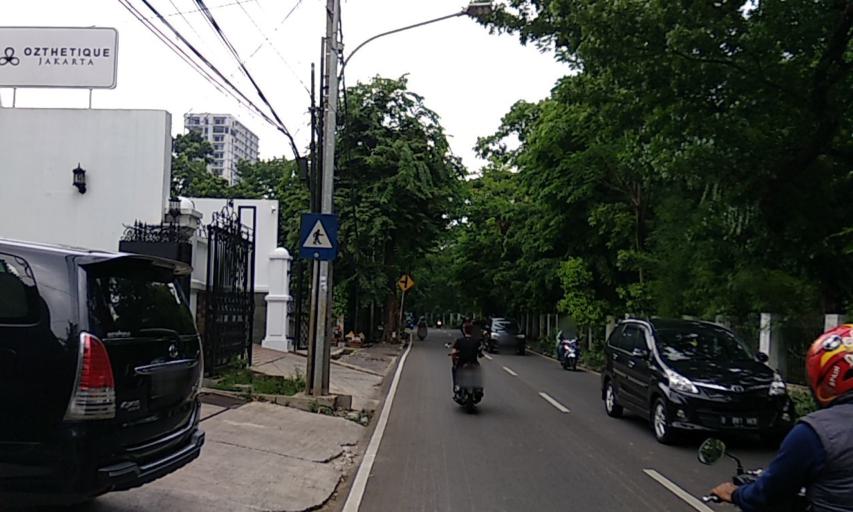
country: ID
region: Jakarta Raya
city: Jakarta
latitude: -6.2398
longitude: 106.8530
